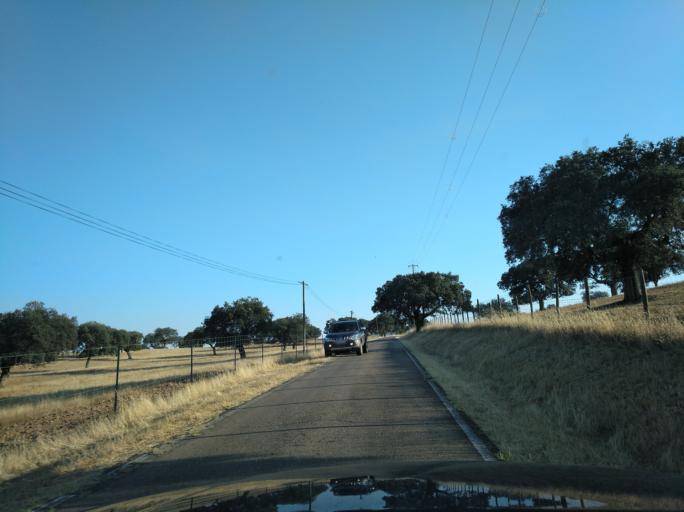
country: PT
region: Portalegre
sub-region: Campo Maior
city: Campo Maior
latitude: 39.0725
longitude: -7.1154
